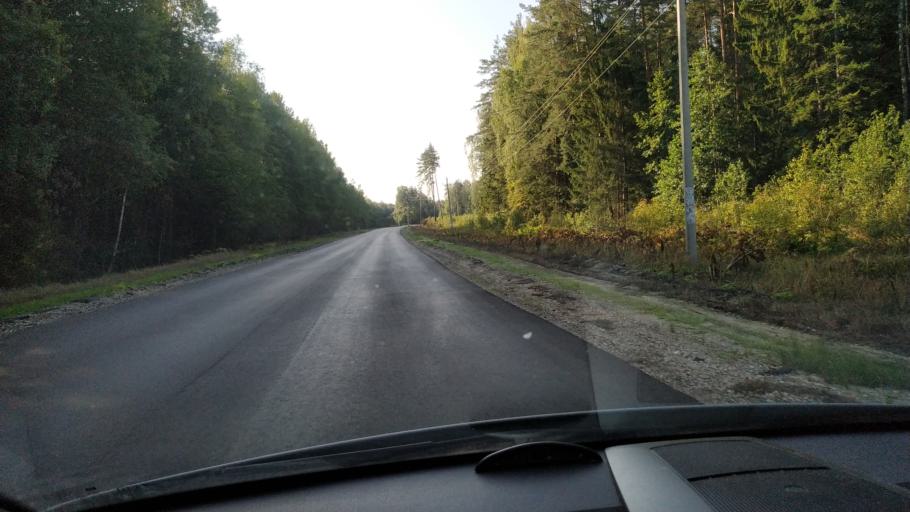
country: RU
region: Moskovskaya
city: Dmitrovskiy Pogost
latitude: 55.4216
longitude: 39.7420
